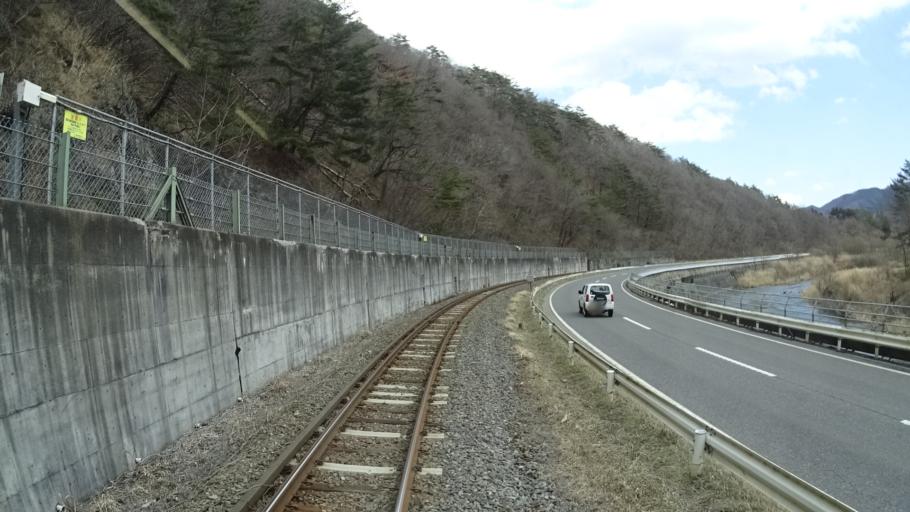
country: JP
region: Iwate
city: Tono
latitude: 39.3038
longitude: 141.3897
